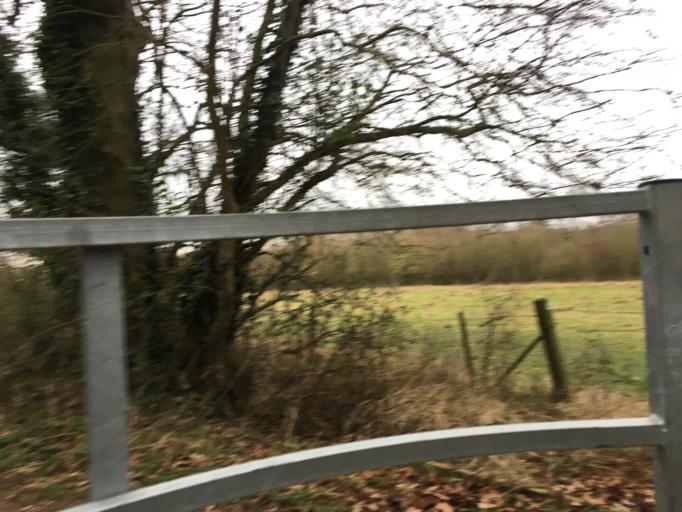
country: GB
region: England
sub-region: Warwickshire
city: Rugby
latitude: 52.3992
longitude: -1.2599
